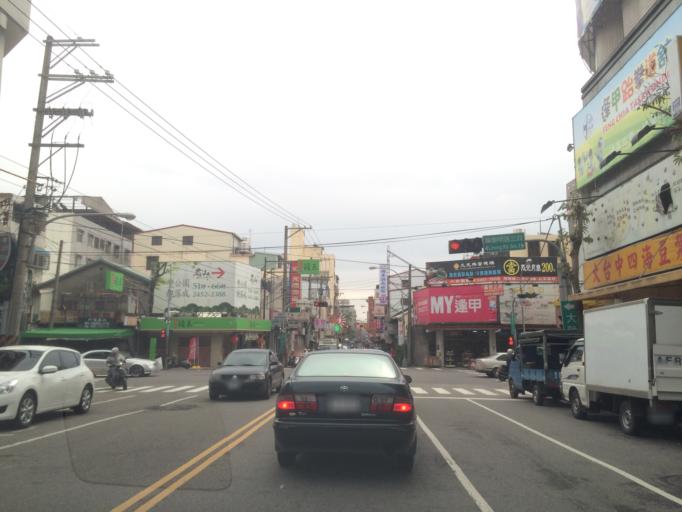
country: TW
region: Taiwan
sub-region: Taichung City
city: Taichung
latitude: 24.1810
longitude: 120.6376
